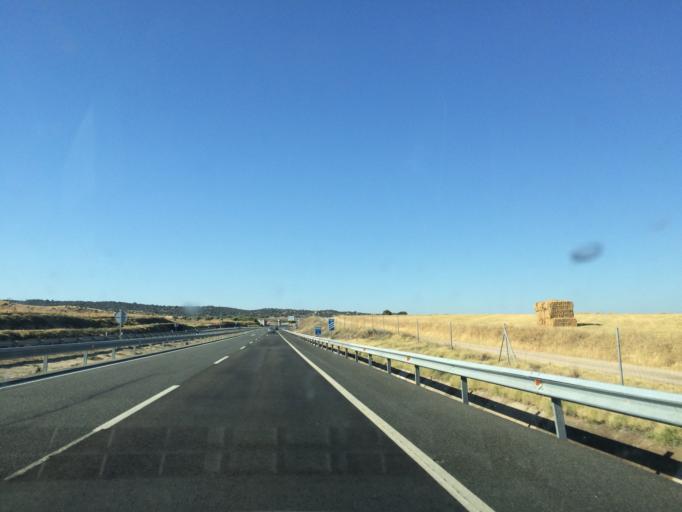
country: ES
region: Castille-La Mancha
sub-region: Province of Toledo
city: Lagartera
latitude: 39.9148
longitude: -5.2093
